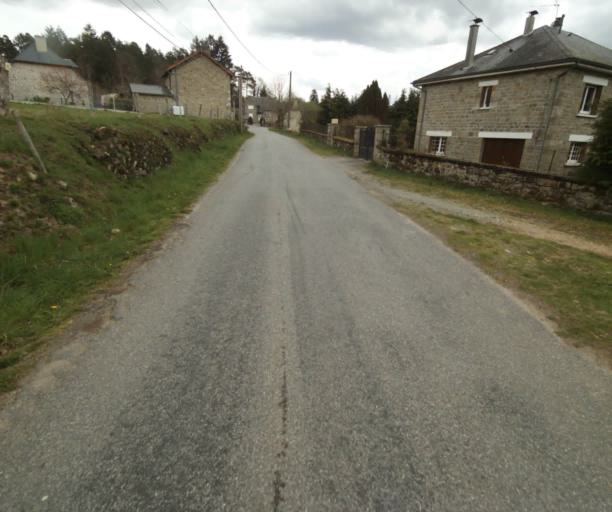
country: FR
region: Limousin
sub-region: Departement de la Correze
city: Correze
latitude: 45.3173
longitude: 1.9259
